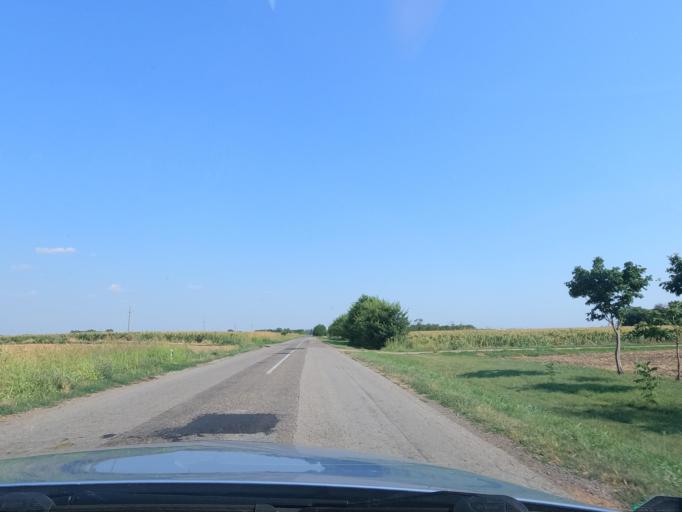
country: RS
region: Autonomna Pokrajina Vojvodina
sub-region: Juznobacki Okrug
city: Becej
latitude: 45.6395
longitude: 19.9990
